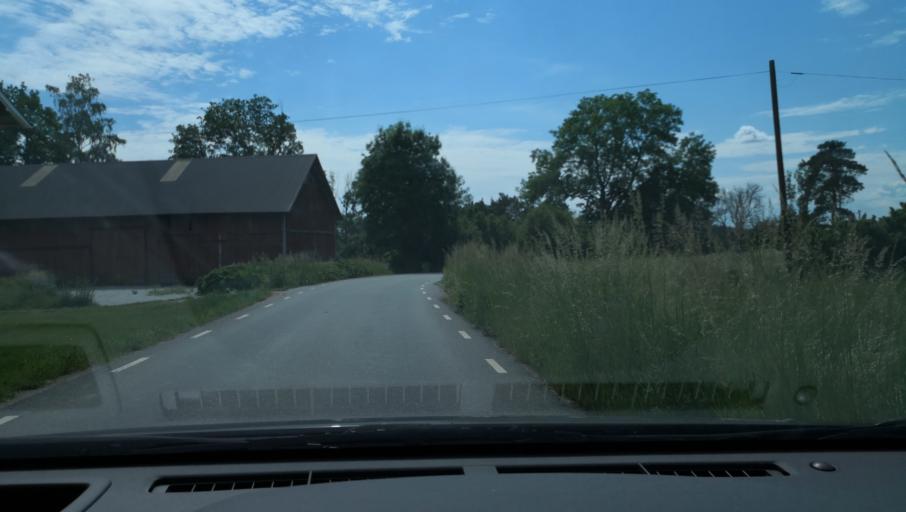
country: SE
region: Uppsala
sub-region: Habo Kommun
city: Balsta
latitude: 59.6952
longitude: 17.4801
